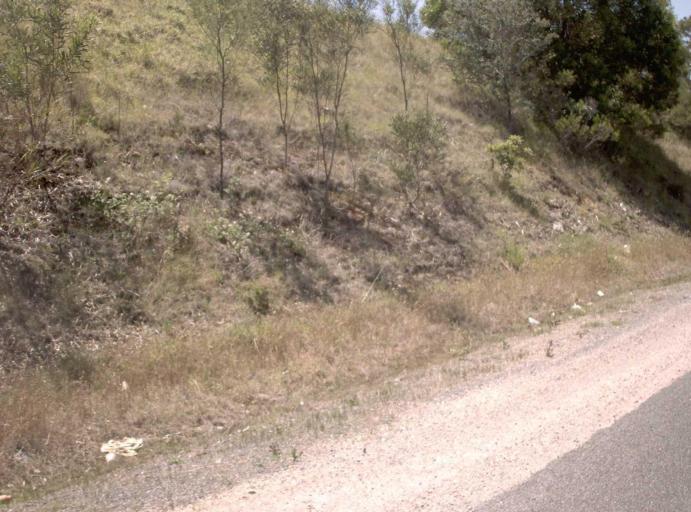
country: AU
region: Victoria
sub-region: East Gippsland
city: Lakes Entrance
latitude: -37.7030
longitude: 148.5564
